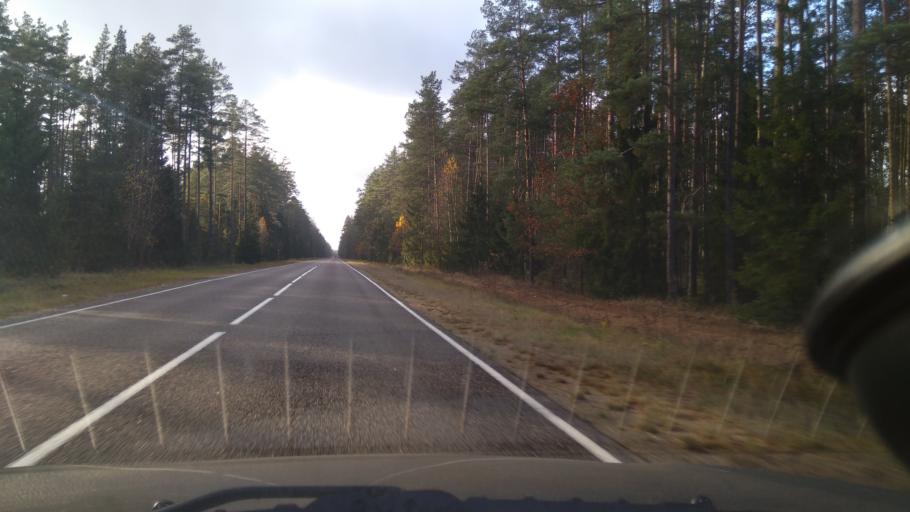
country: BY
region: Minsk
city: Urechcha
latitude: 53.2167
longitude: 27.8354
